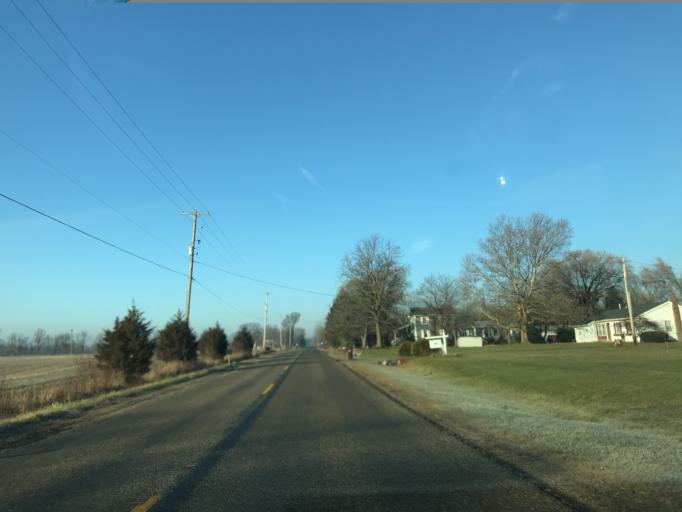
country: US
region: Michigan
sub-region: Eaton County
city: Dimondale
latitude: 42.6620
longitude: -84.6275
